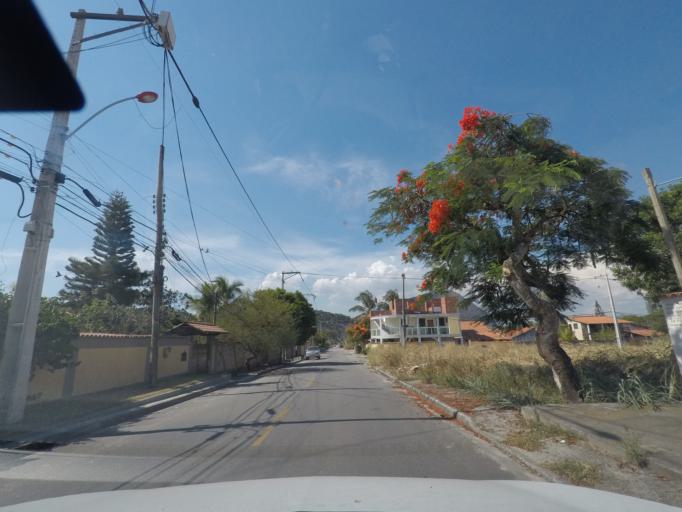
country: BR
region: Rio de Janeiro
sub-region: Niteroi
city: Niteroi
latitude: -22.9633
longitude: -42.9703
